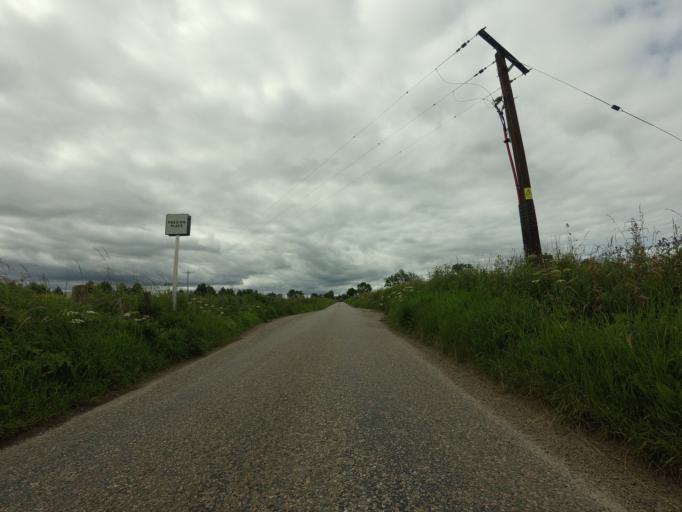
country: GB
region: Scotland
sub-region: Moray
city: Forres
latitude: 57.6180
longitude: -3.6179
